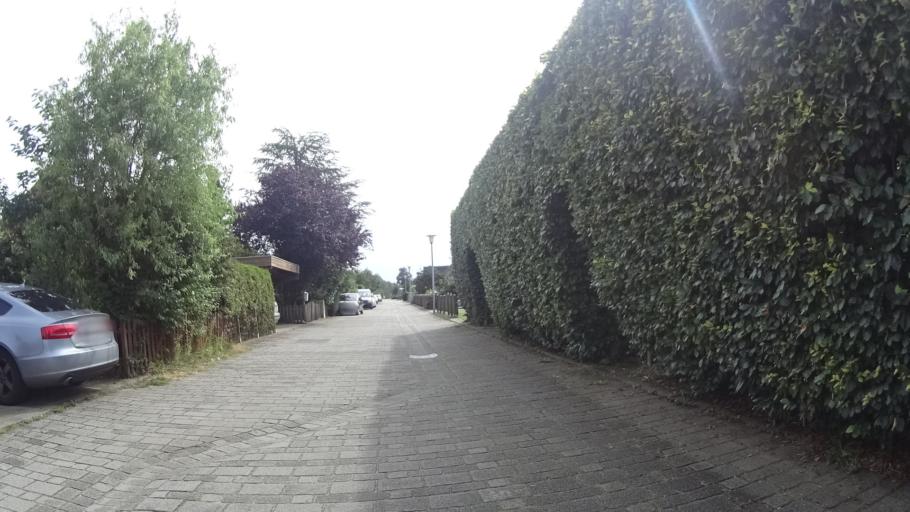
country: DE
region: Schleswig-Holstein
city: Henstedt-Ulzburg
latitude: 53.7586
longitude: 9.9998
